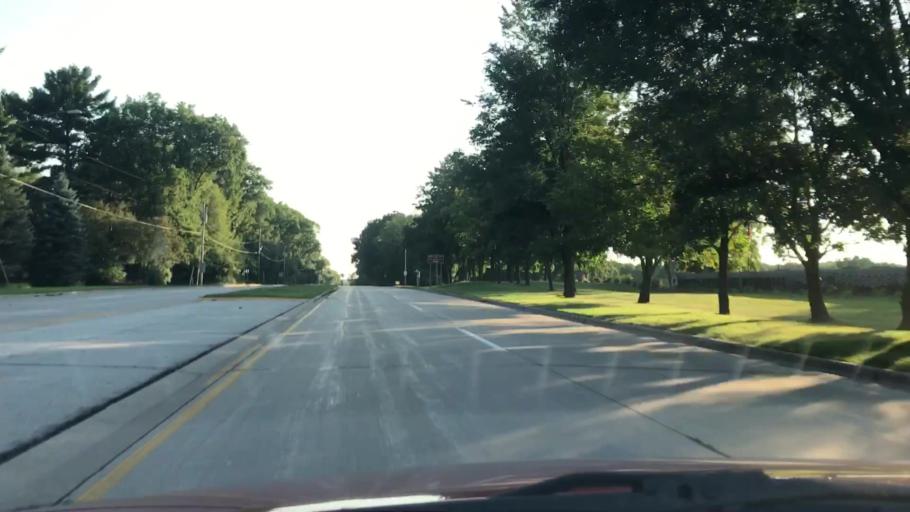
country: US
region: Wisconsin
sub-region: Brown County
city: Howard
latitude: 44.5212
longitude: -88.1332
